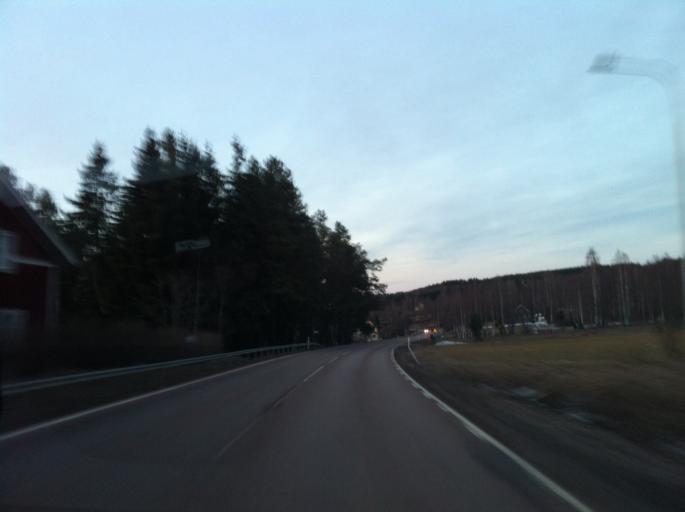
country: SE
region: Dalarna
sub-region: Orsa Kommun
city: Orsa
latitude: 61.0679
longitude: 14.6154
